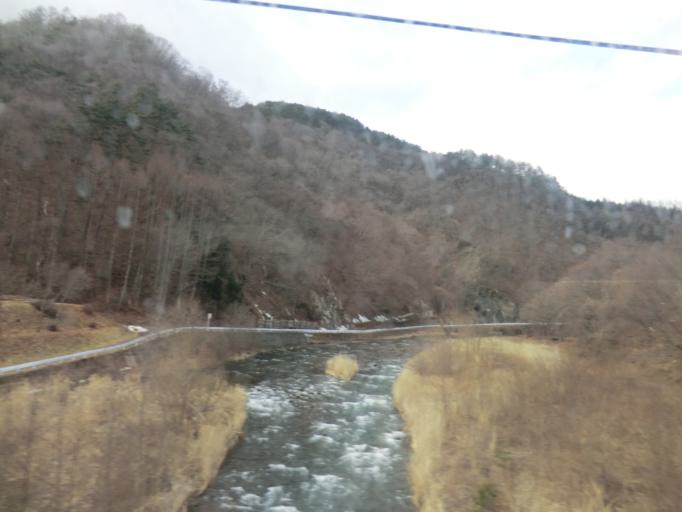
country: JP
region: Nagano
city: Ina
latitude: 35.9186
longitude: 137.7699
